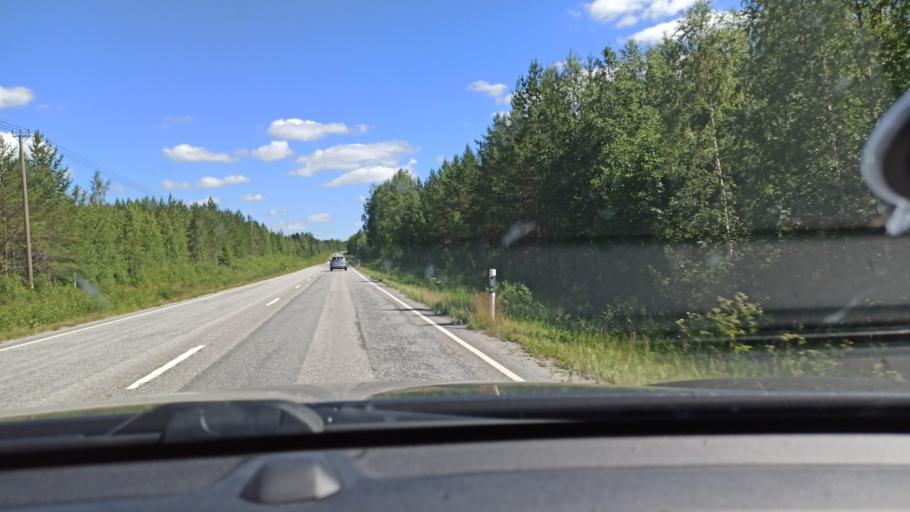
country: FI
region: Ostrobothnia
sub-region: Vaasa
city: Malax
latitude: 62.9672
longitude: 21.5852
